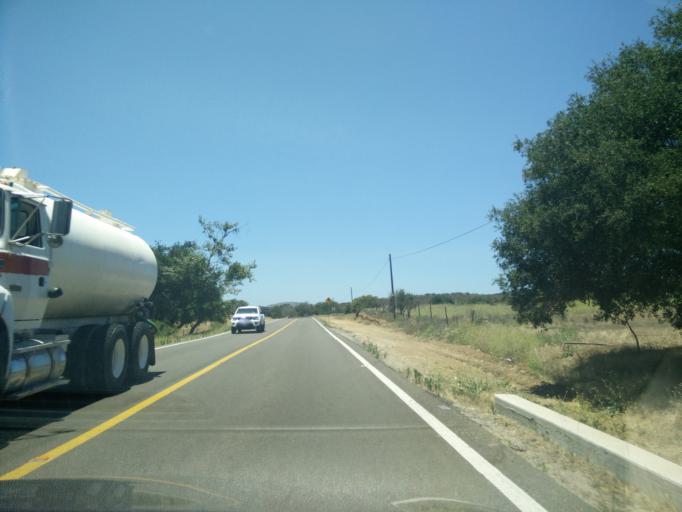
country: MX
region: Baja California
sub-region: Ensenada
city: Rancho Verde
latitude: 31.9933
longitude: -116.6455
